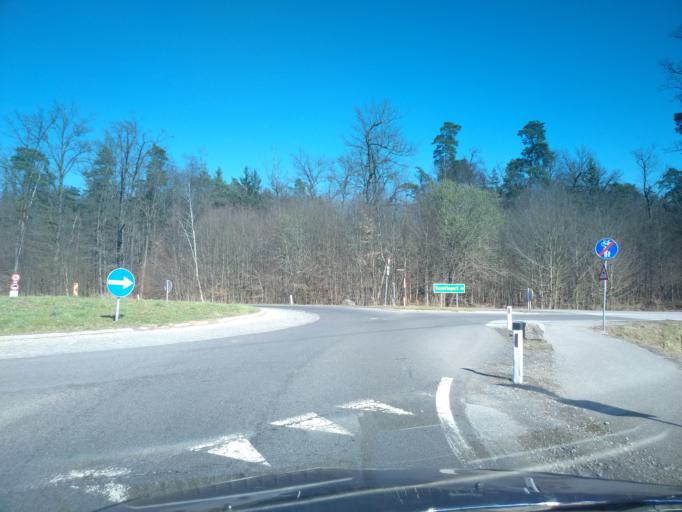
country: AT
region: Styria
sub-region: Politischer Bezirk Graz-Umgebung
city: Wundschuh
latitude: 46.9341
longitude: 15.4678
